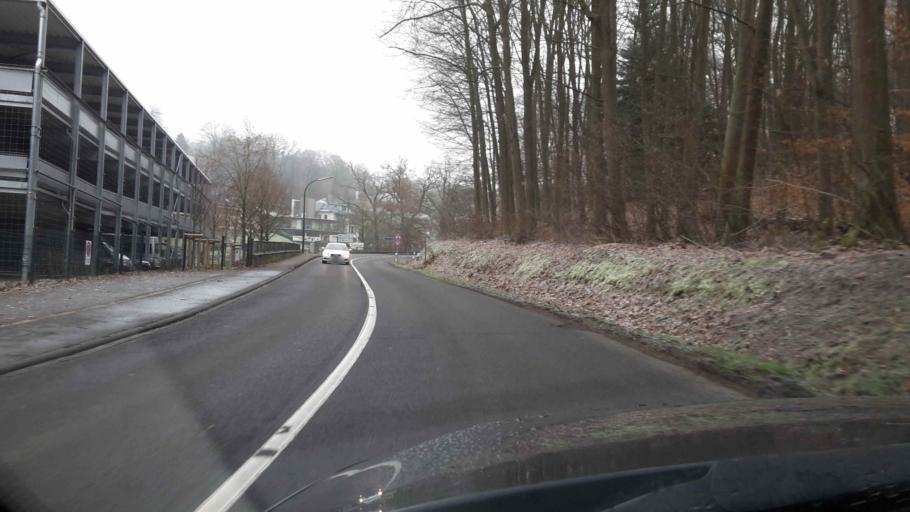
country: DE
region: North Rhine-Westphalia
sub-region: Regierungsbezirk Koln
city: Hennef
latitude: 50.7630
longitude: 7.2713
